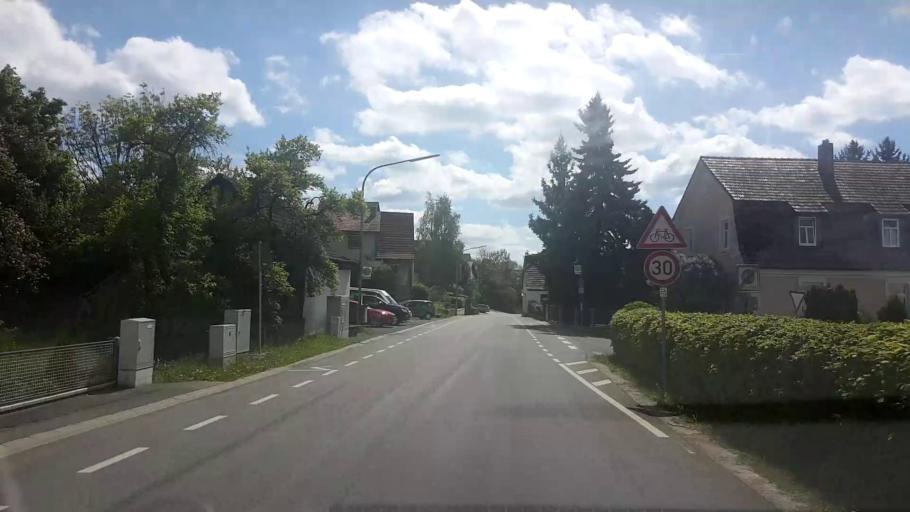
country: DE
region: Bavaria
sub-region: Upper Franconia
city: Grossheirath
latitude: 50.1651
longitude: 10.9376
